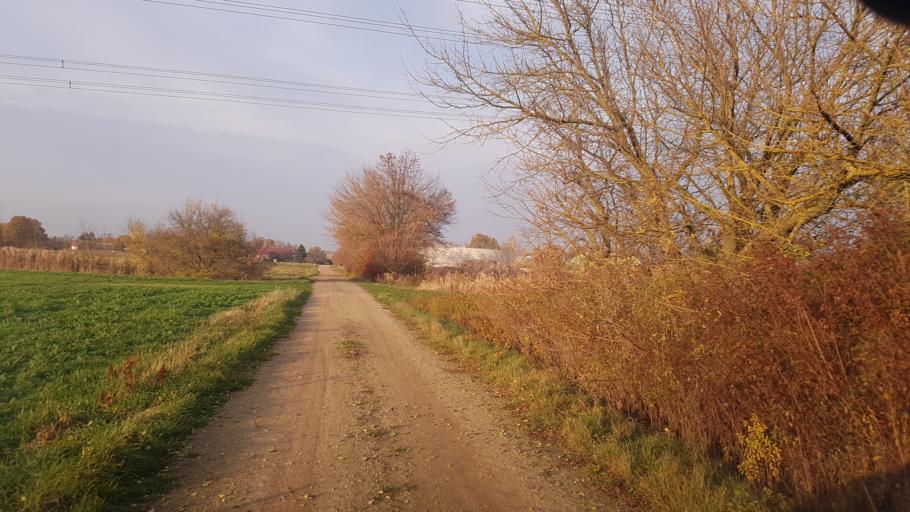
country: DE
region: Brandenburg
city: Schonewalde
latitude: 51.6529
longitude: 13.5988
